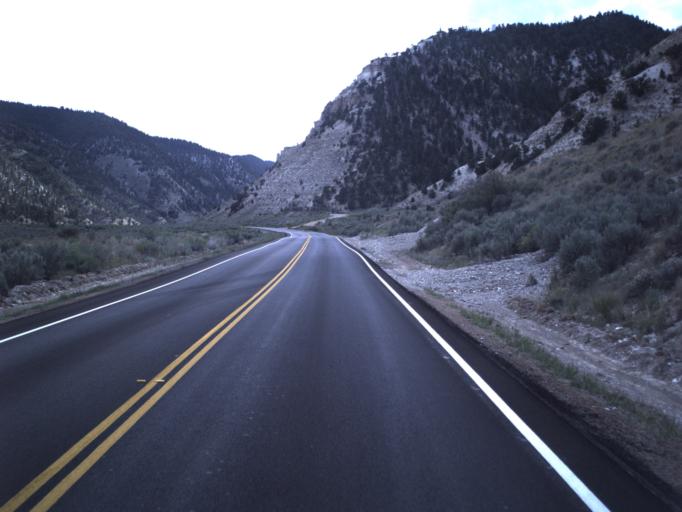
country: US
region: Utah
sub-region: Duchesne County
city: Duchesne
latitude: 40.0243
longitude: -110.5557
